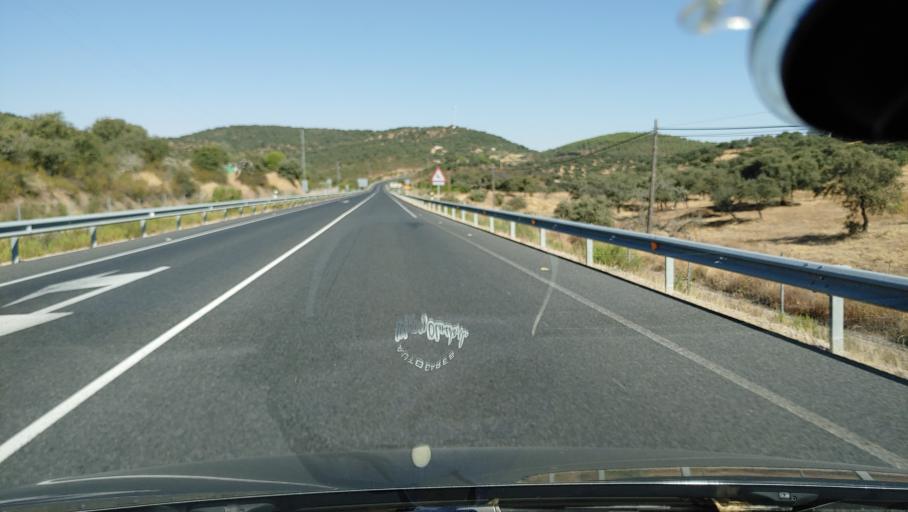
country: ES
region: Andalusia
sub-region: Province of Cordoba
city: Villaharta
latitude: 38.0990
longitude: -4.8739
